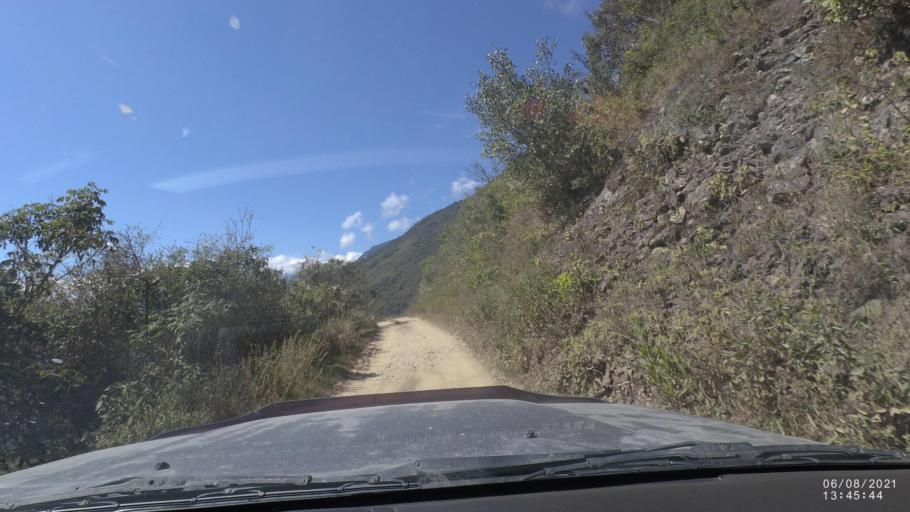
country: BO
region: La Paz
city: Quime
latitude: -16.6709
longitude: -66.7309
